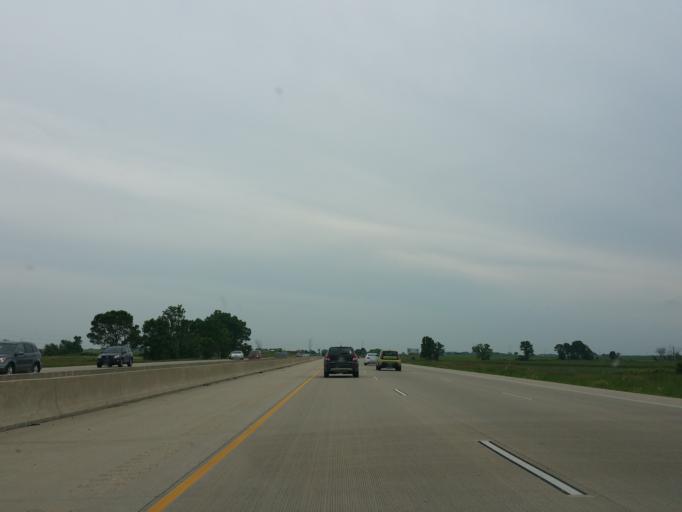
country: US
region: Wisconsin
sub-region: Dane County
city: De Forest
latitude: 43.2964
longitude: -89.4202
